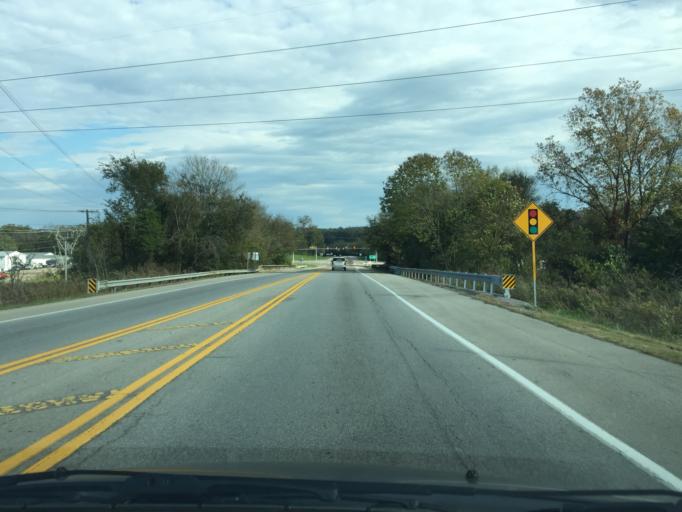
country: US
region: Tennessee
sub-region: Loudon County
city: Loudon
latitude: 35.7190
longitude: -84.3614
